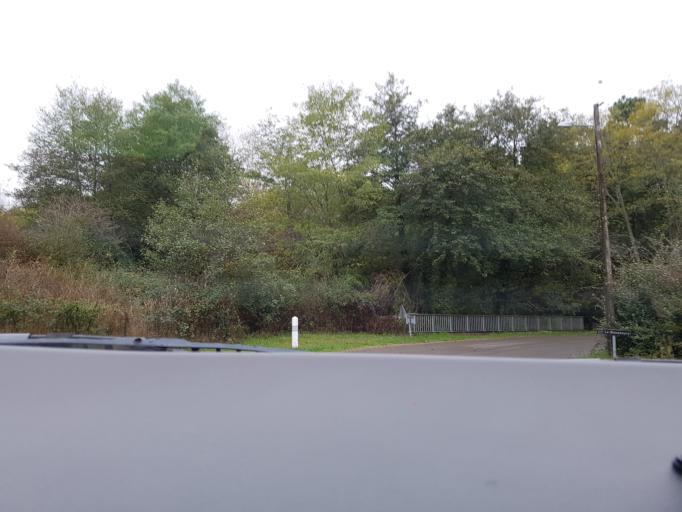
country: FR
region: Aquitaine
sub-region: Departement des Landes
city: Roquefort
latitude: 44.1005
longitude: -0.4063
